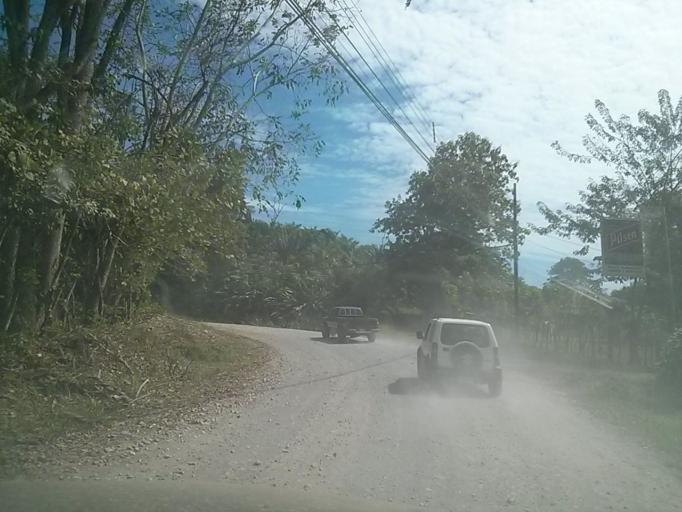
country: CR
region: Puntarenas
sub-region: Canton de Golfito
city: Golfito
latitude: 8.4539
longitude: -83.0533
